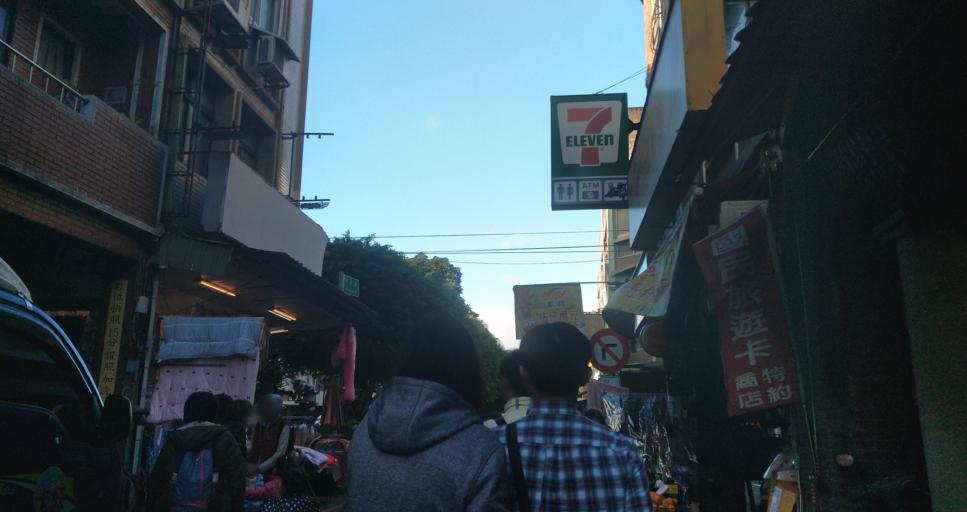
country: TW
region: Taiwan
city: Daxi
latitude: 24.8827
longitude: 121.2876
